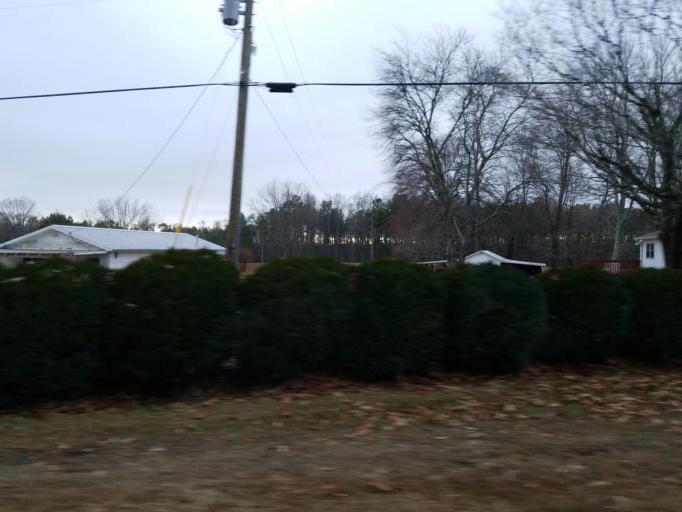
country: US
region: Georgia
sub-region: Dawson County
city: Dawsonville
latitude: 34.4629
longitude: -84.1455
